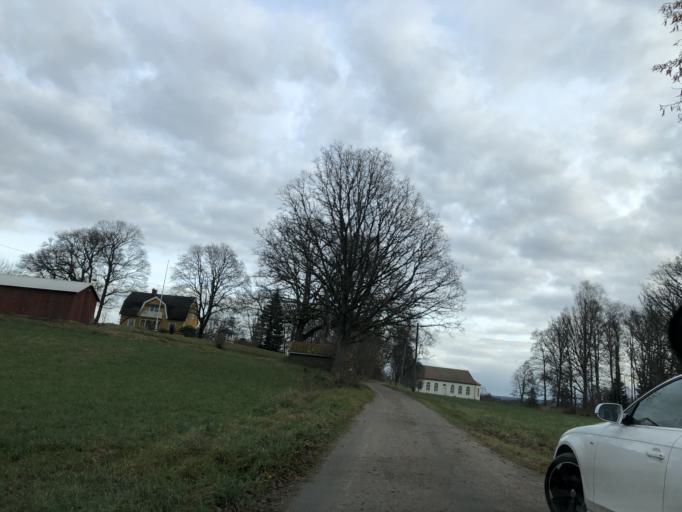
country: SE
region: Vaestra Goetaland
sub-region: Ulricehamns Kommun
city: Ulricehamn
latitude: 57.7241
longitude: 13.3097
